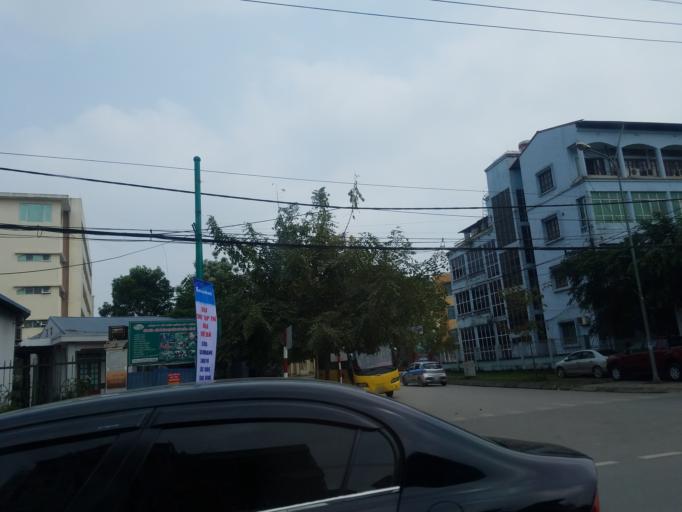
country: VN
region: Thai Nguyen
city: Thanh Pho Thai Nguyen
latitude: 21.5849
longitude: 105.8402
